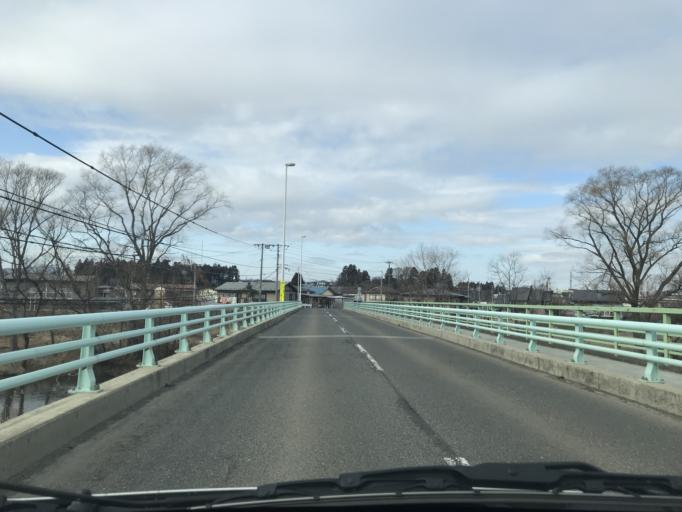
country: JP
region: Iwate
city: Hanamaki
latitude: 39.3787
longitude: 141.1065
